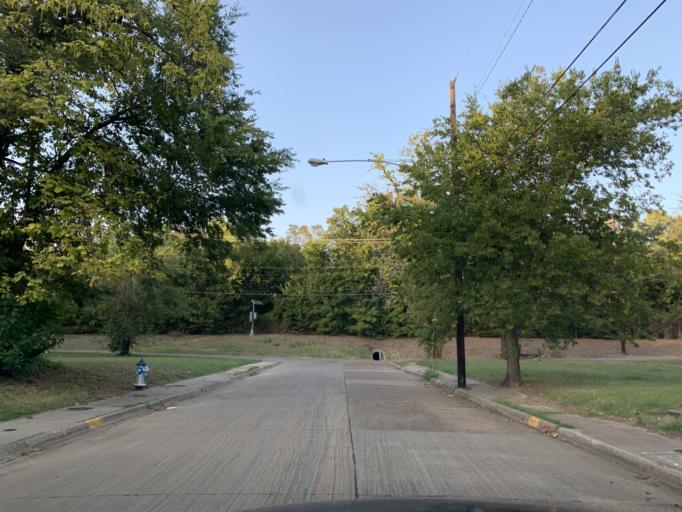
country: US
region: Texas
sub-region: Dallas County
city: Dallas
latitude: 32.7534
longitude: -96.7470
